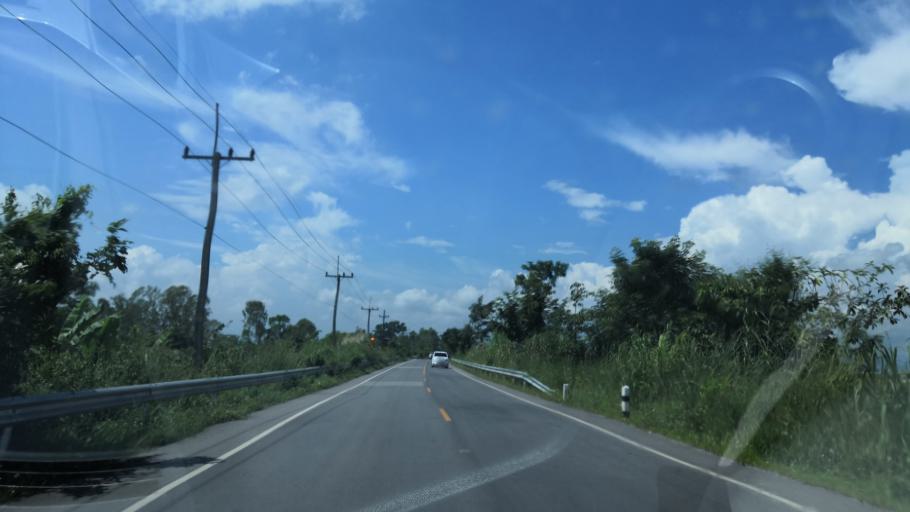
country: TH
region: Chiang Rai
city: Wiang Chiang Rung
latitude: 19.9653
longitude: 99.9946
